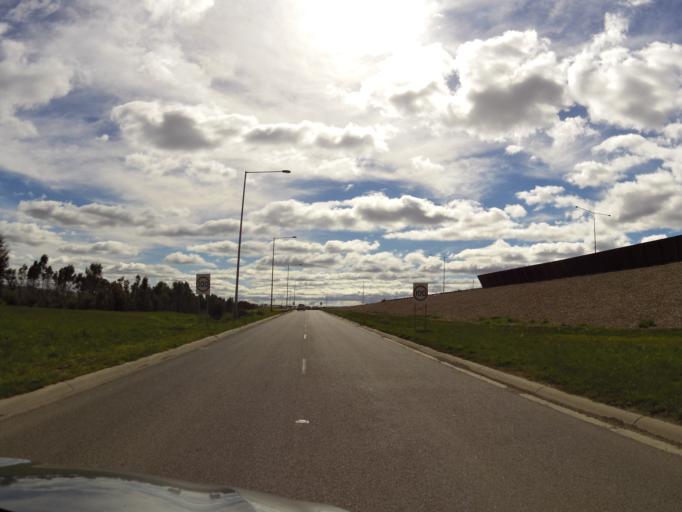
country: AU
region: Victoria
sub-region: Whittlesea
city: Lalor
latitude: -37.6477
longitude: 144.9900
